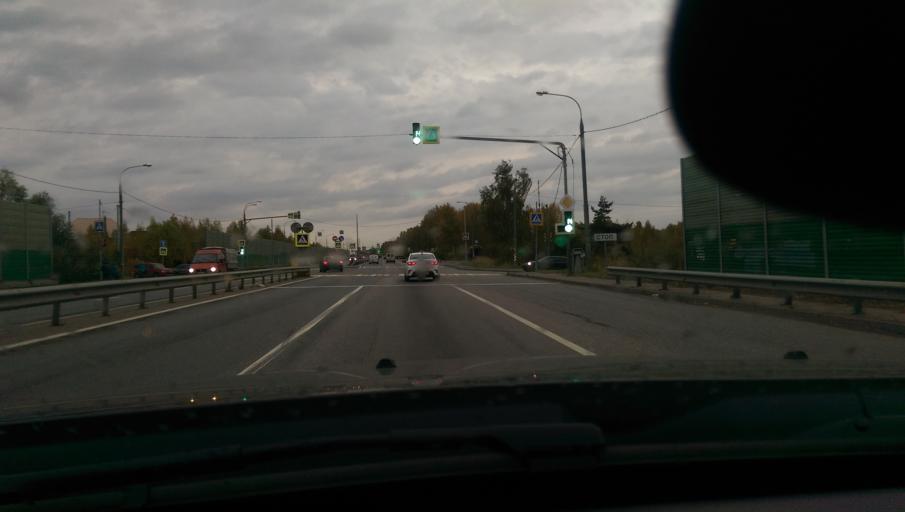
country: RU
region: Moskovskaya
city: Povedniki
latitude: 55.9453
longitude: 37.6546
